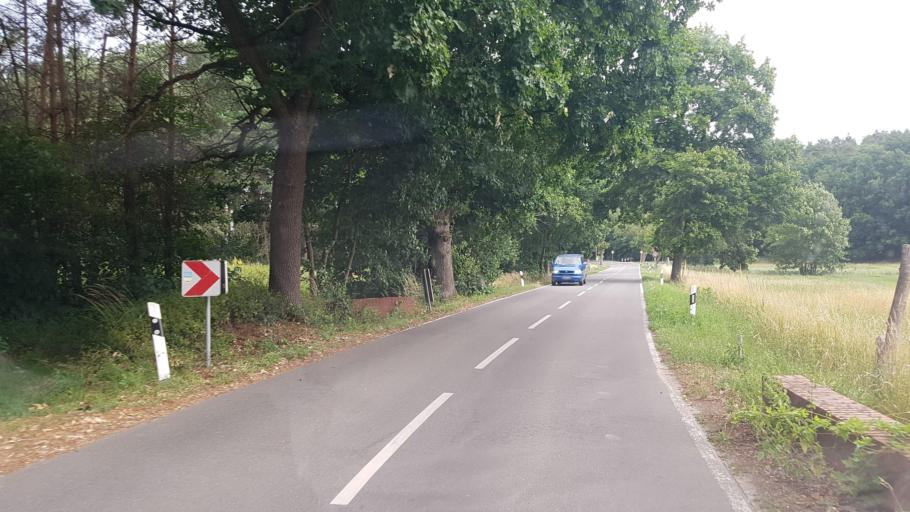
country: DE
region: Saxony-Anhalt
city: Kropstadt
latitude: 51.9413
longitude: 12.7062
